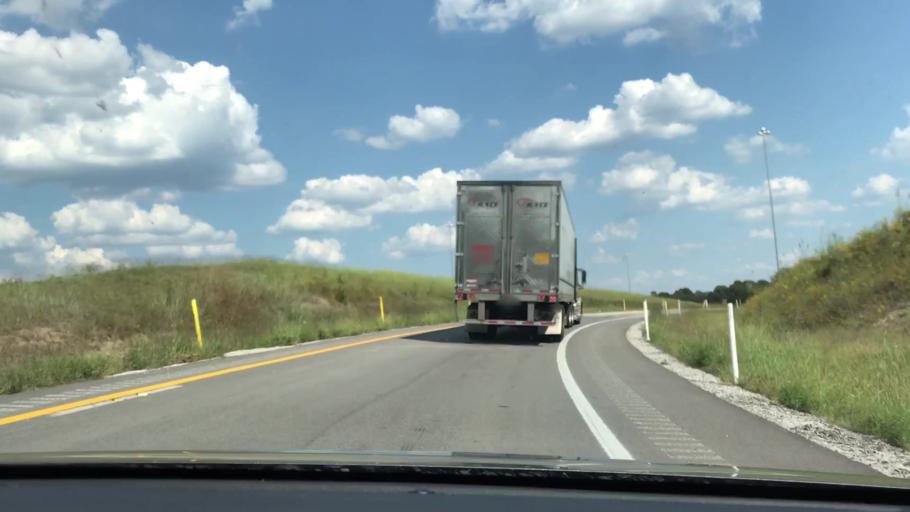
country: US
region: Kentucky
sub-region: Ohio County
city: Beaver Dam
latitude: 37.3824
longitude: -86.8127
